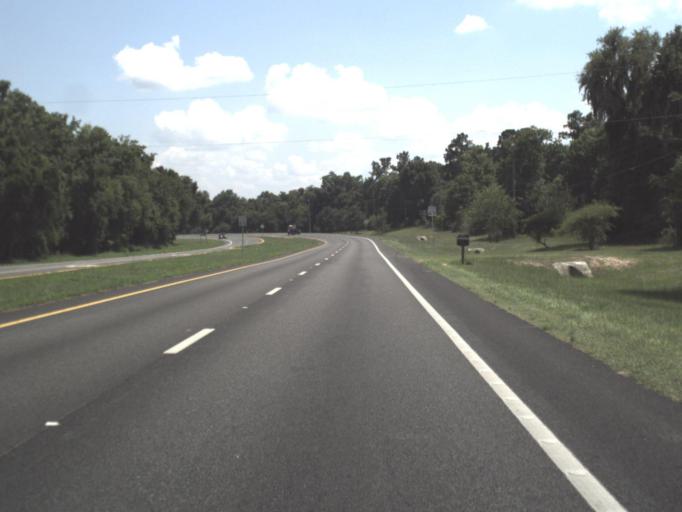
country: US
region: Florida
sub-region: Alachua County
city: Gainesville
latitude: 29.6177
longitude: -82.2559
